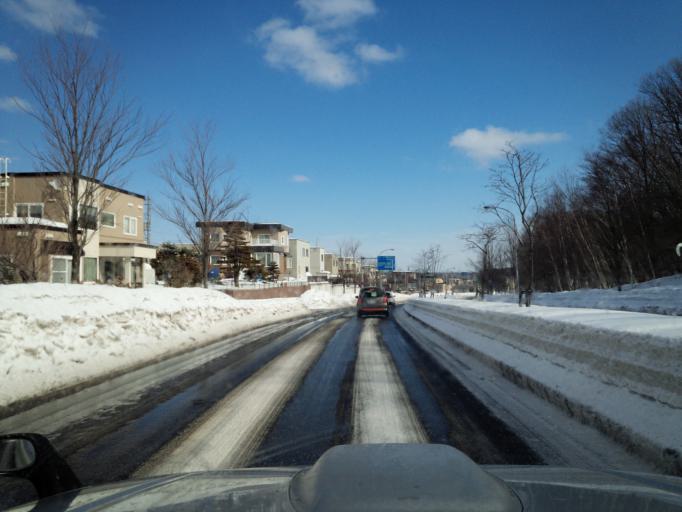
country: JP
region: Hokkaido
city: Kitahiroshima
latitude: 43.0061
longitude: 141.4611
